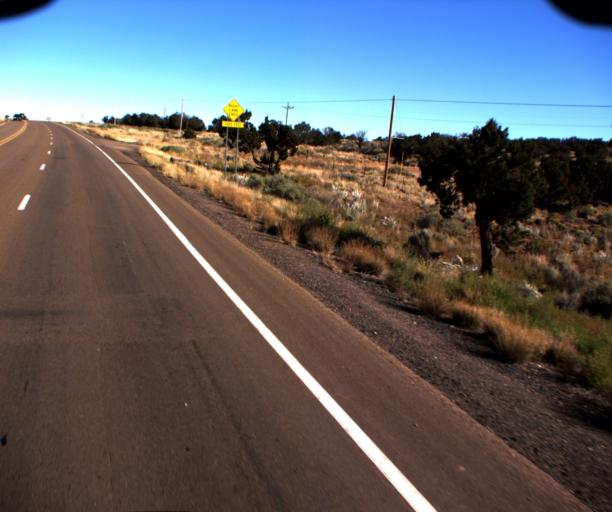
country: US
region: Arizona
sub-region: Navajo County
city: Snowflake
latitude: 34.5402
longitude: -110.0794
